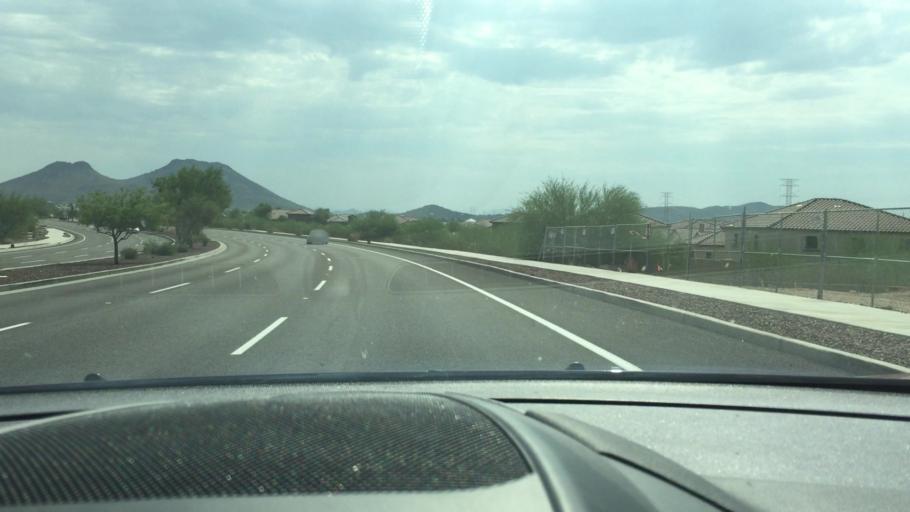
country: US
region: Arizona
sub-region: Maricopa County
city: Sun City West
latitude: 33.7086
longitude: -112.2338
